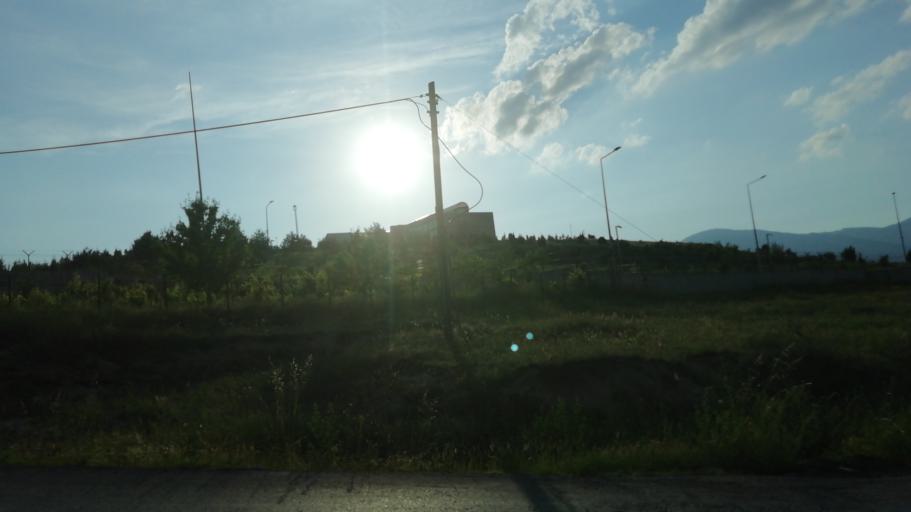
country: TR
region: Karabuk
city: Karabuk
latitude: 41.1346
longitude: 32.6333
